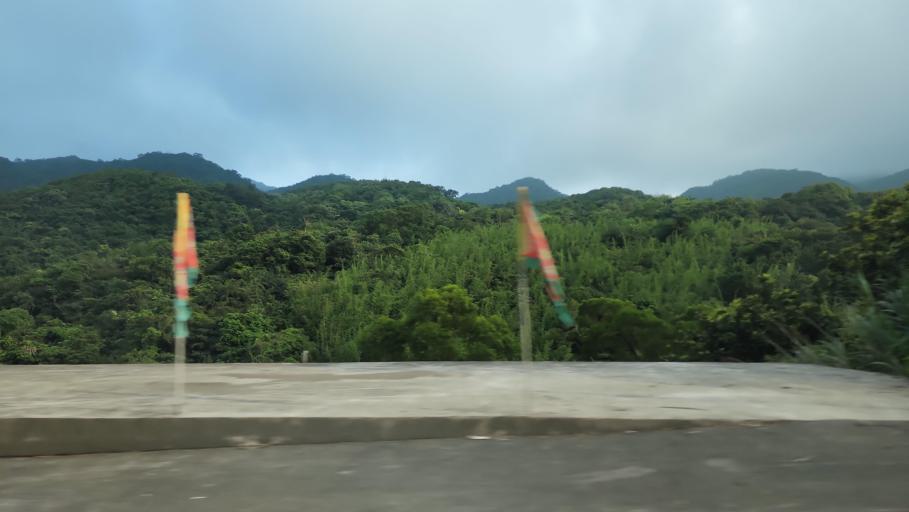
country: TW
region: Taiwan
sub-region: Keelung
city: Keelung
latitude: 25.1601
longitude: 121.6494
